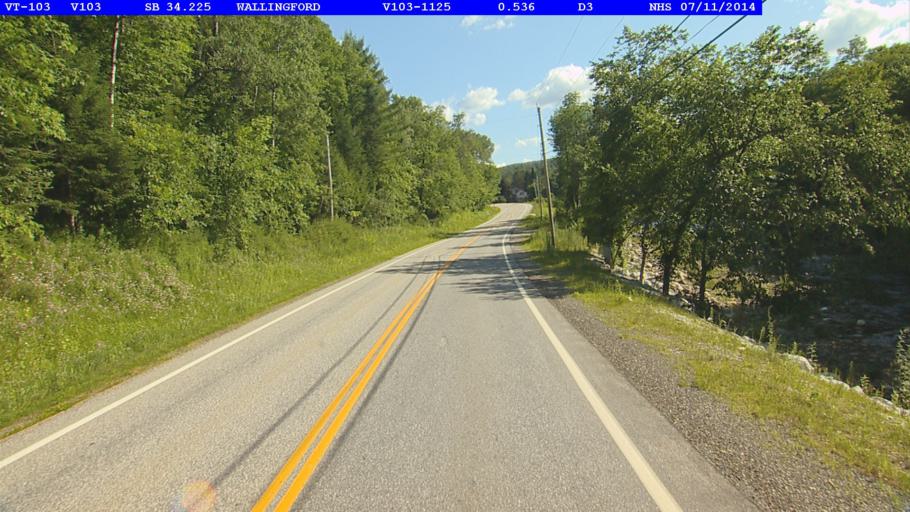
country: US
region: Vermont
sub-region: Rutland County
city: Rutland
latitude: 43.4579
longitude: -72.8753
